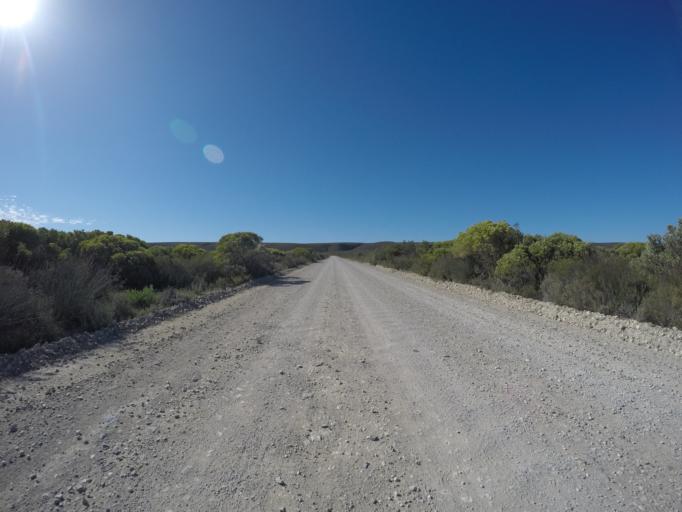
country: ZA
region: Western Cape
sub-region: Overberg District Municipality
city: Bredasdorp
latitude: -34.4377
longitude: 20.4205
